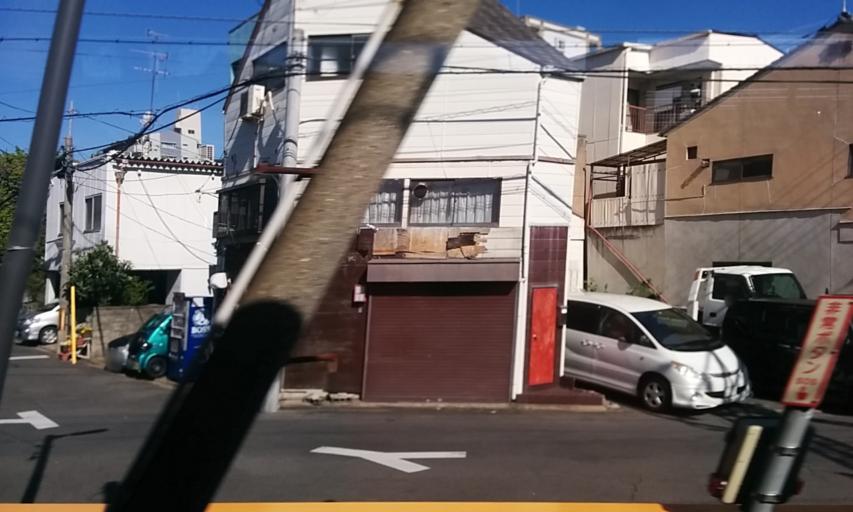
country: JP
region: Kyoto
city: Kyoto
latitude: 34.9986
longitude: 135.7255
